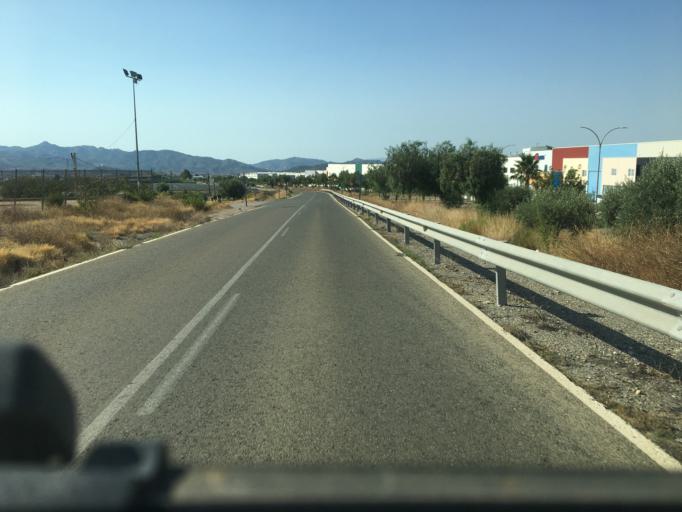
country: ES
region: Andalusia
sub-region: Provincia de Almeria
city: Huercal-Overa
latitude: 37.4202
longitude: -1.9691
